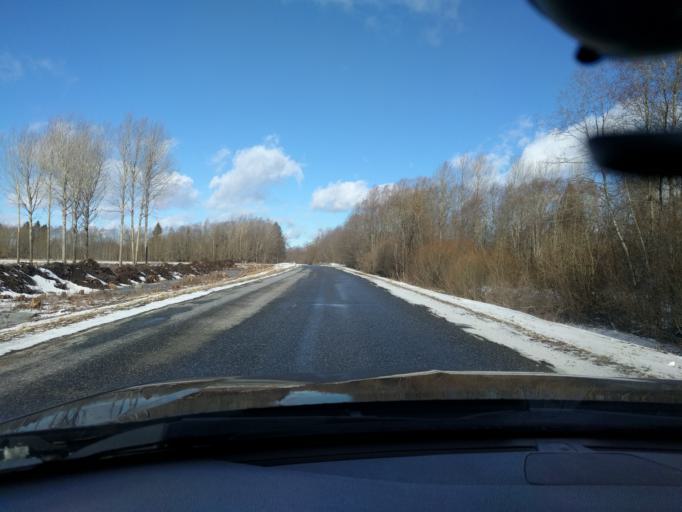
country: EE
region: Harju
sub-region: Raasiku vald
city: Raasiku
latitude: 59.3035
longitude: 25.1712
